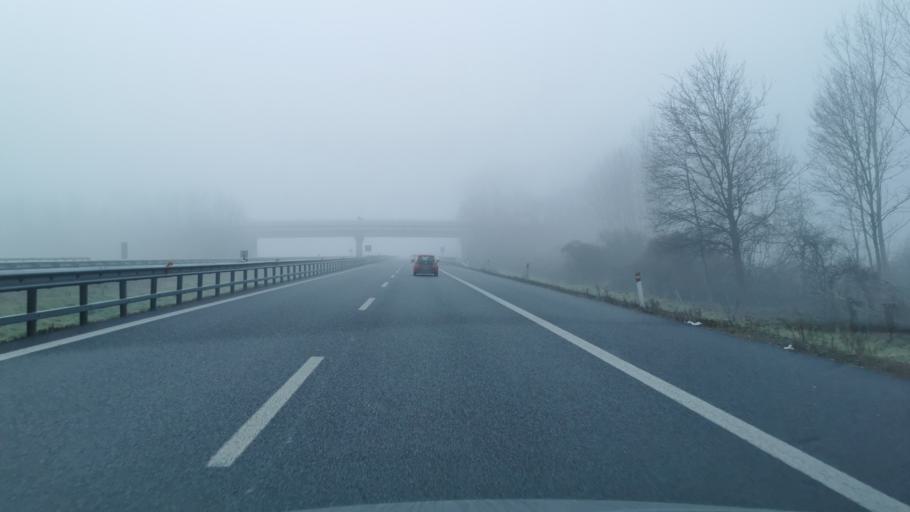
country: IT
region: Piedmont
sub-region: Provincia di Cuneo
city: Caramagna Piemonte
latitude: 44.7722
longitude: 7.7515
